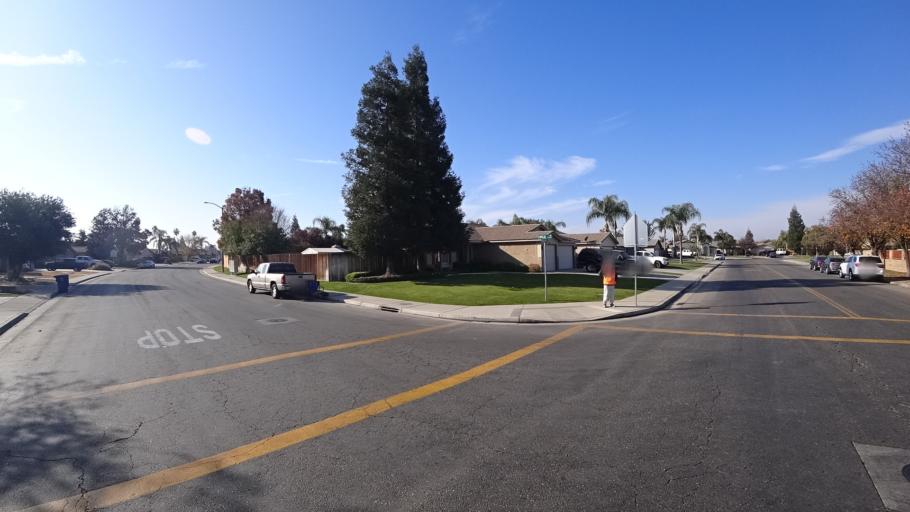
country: US
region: California
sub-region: Kern County
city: Oildale
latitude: 35.4071
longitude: -119.0609
